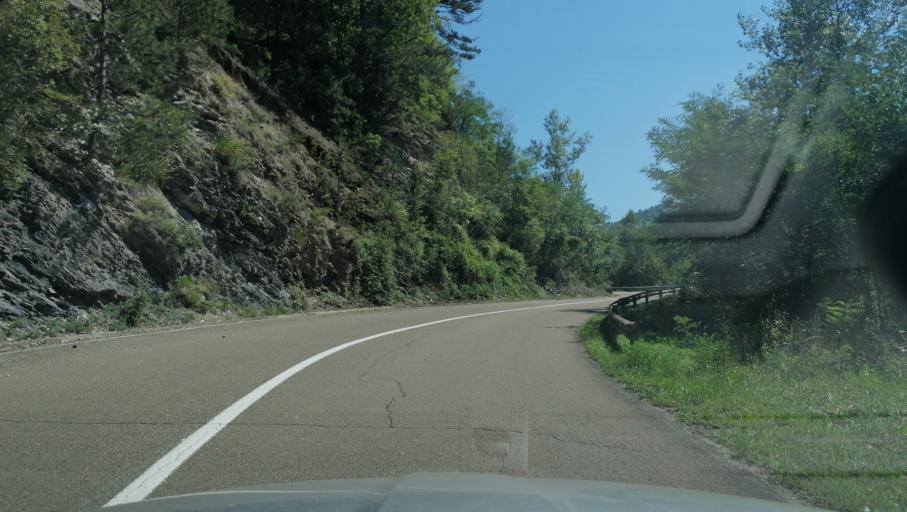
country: RS
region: Central Serbia
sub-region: Raski Okrug
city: Raska
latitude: 43.4718
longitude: 20.5468
